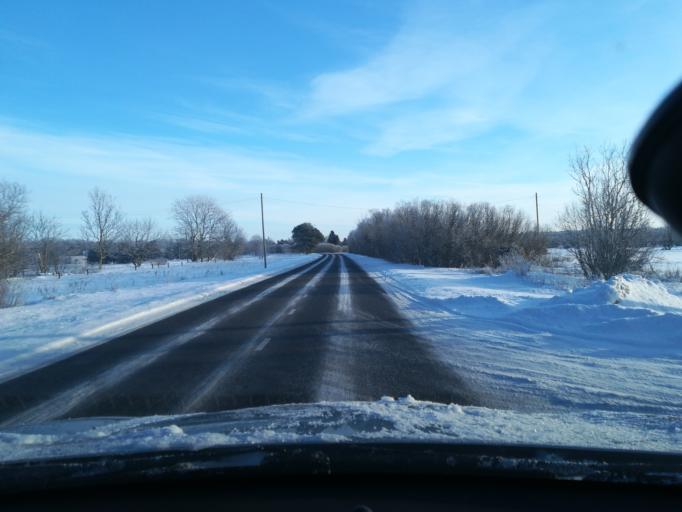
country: EE
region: Harju
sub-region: Keila linn
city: Keila
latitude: 59.3893
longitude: 24.4020
